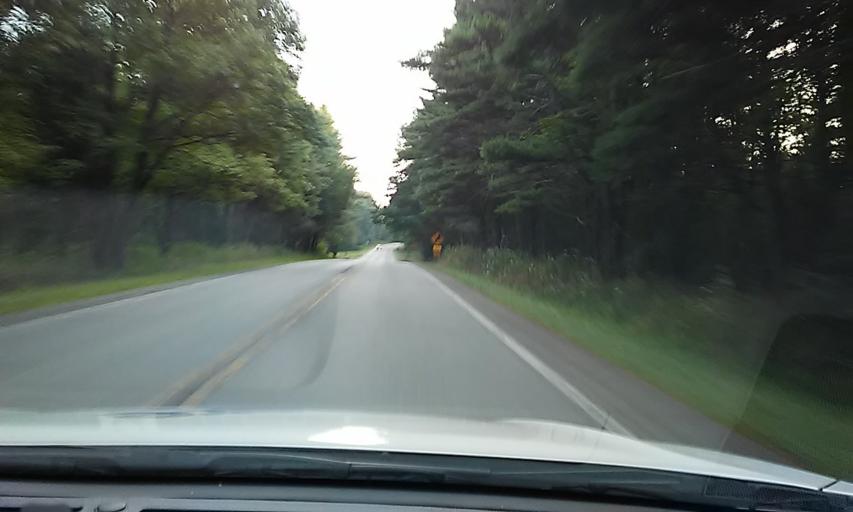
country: US
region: Pennsylvania
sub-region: Forest County
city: Marienville
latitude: 41.4137
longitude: -79.2199
